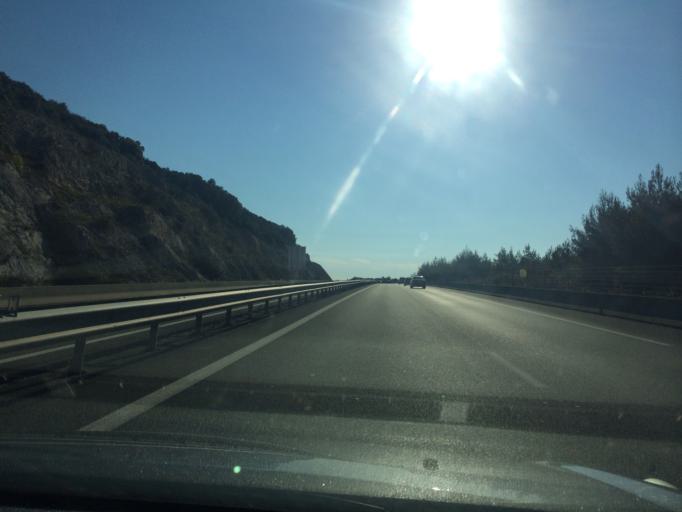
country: FR
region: Languedoc-Roussillon
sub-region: Departement de l'Herault
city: Montarnaud
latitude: 43.6279
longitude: 3.6710
